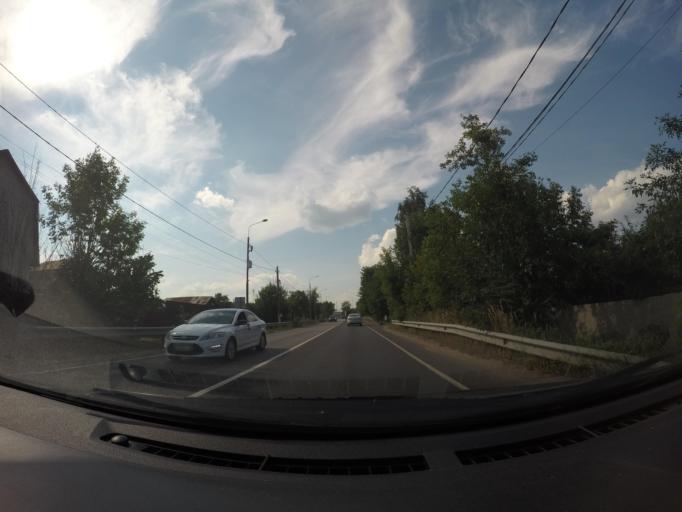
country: RU
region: Moskovskaya
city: Gzhel'
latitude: 55.6247
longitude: 38.3724
